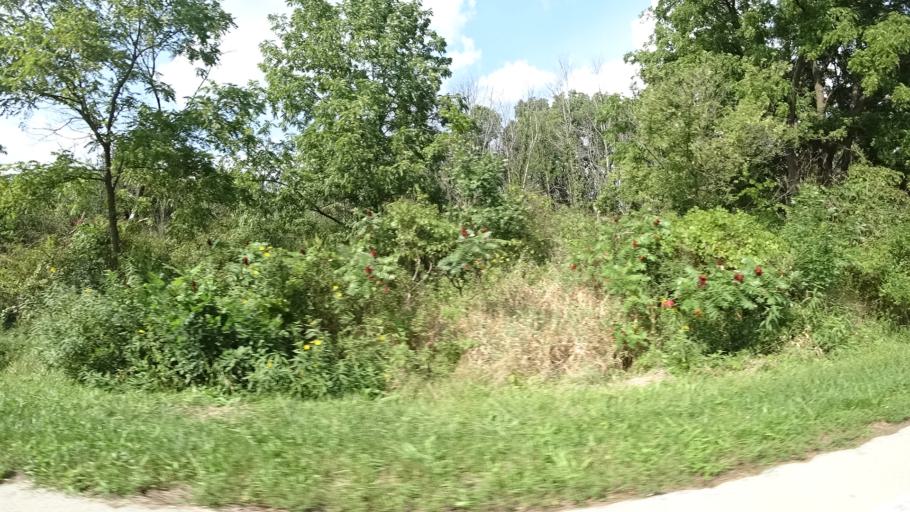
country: US
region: Illinois
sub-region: Will County
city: Goodings Grove
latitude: 41.6511
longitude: -87.9184
